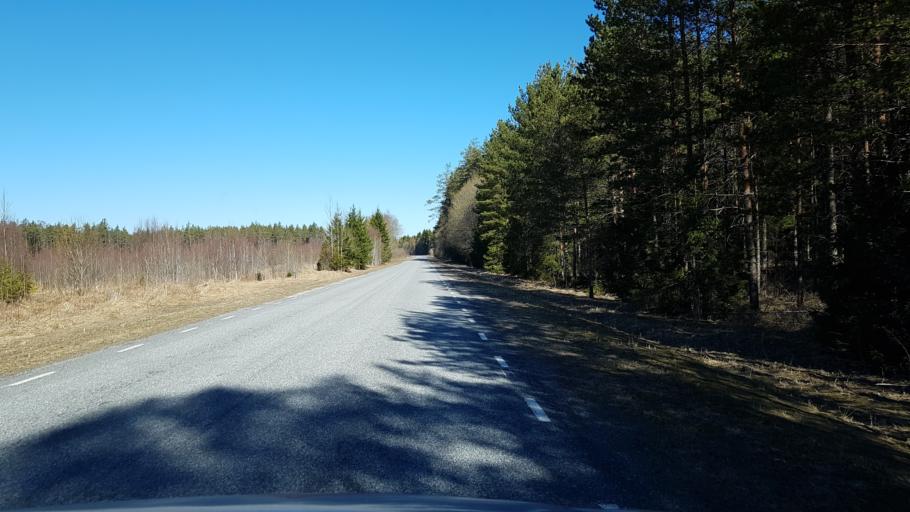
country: EE
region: Laeaene-Virumaa
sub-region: Haljala vald
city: Haljala
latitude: 59.5018
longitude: 26.2393
